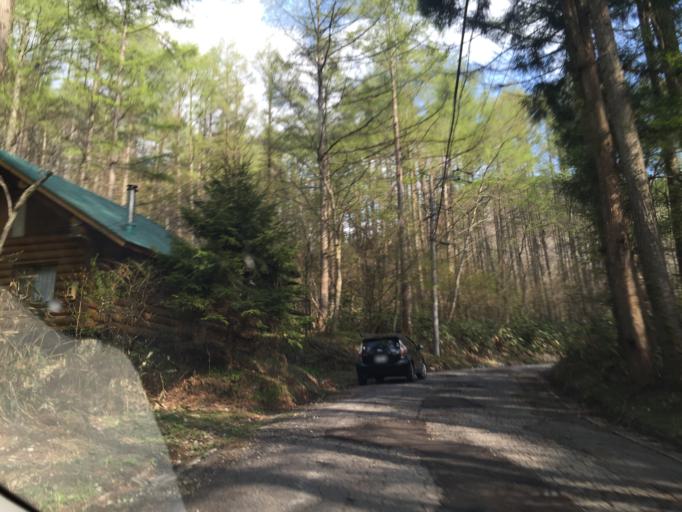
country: JP
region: Nagano
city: Iida
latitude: 35.3535
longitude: 137.6773
